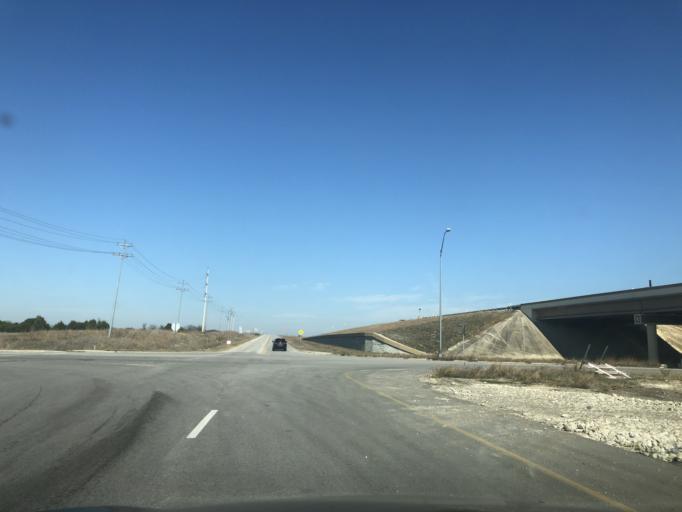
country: US
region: Texas
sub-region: Travis County
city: Manor
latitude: 30.3695
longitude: -97.5842
